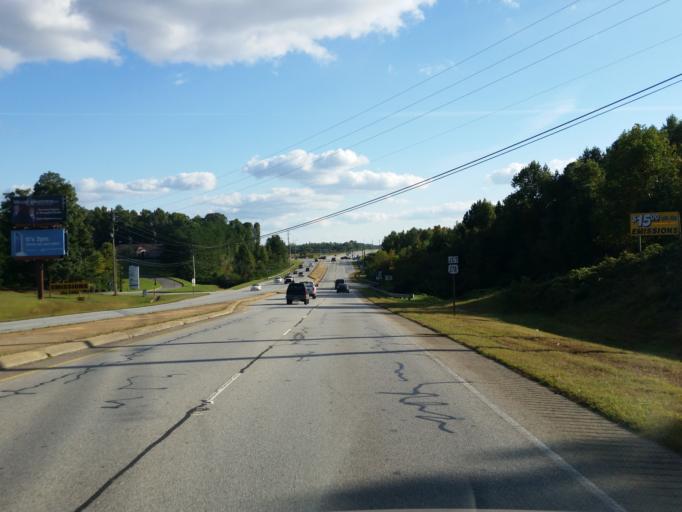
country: US
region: Georgia
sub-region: Paulding County
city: Hiram
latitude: 33.9066
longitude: -84.7790
